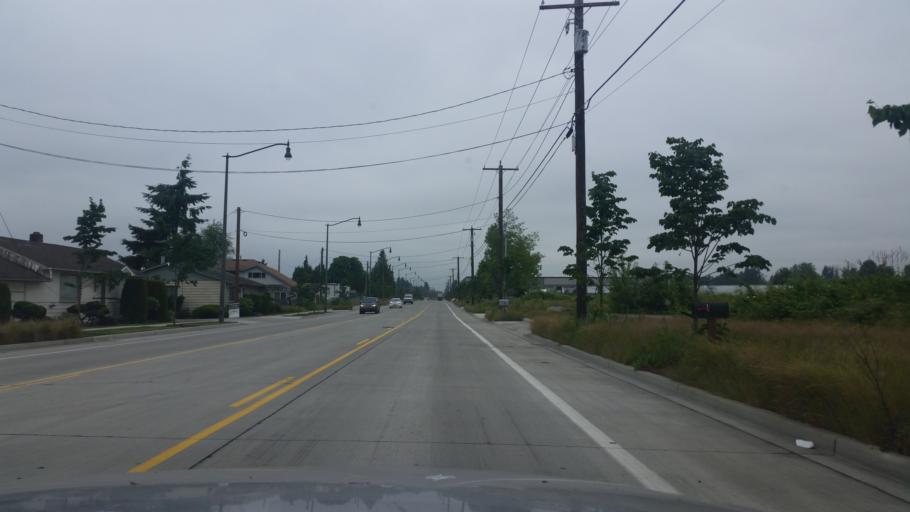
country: US
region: Washington
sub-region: King County
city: Pacific
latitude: 47.2380
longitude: -122.2487
